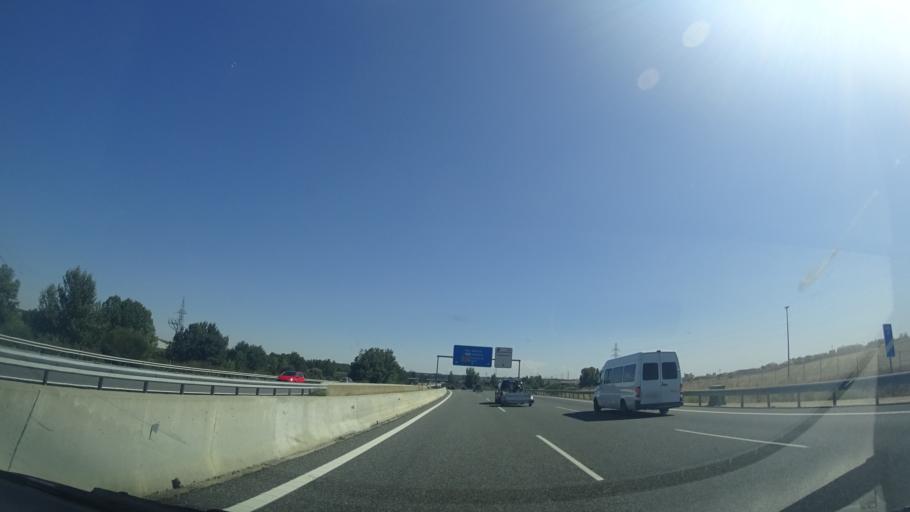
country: ES
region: Castille and Leon
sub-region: Provincia de Zamora
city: Benavente
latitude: 42.0208
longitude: -5.6691
